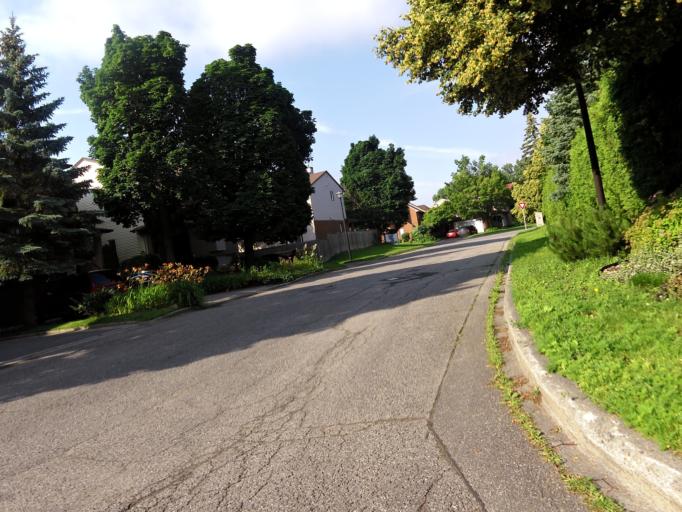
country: CA
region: Ontario
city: Ottawa
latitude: 45.3449
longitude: -75.6886
